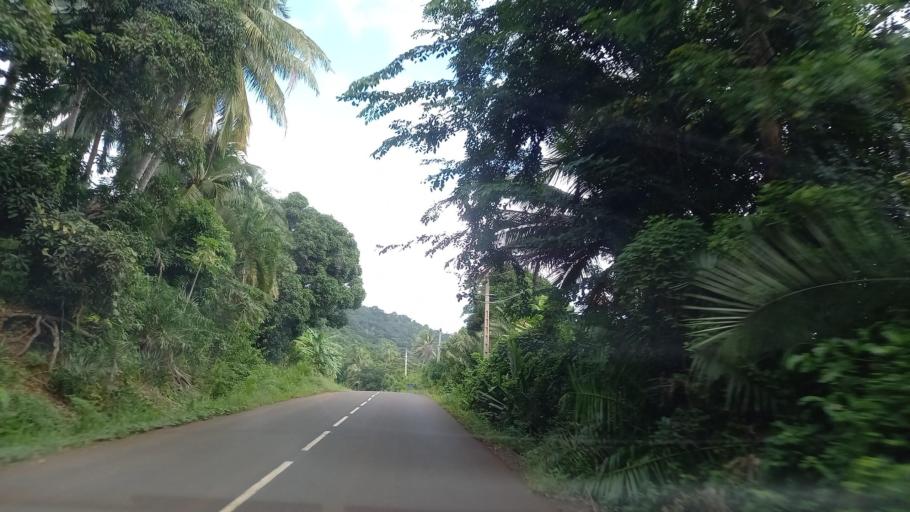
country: YT
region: Kani-Keli
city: Kani Keli
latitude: -12.9407
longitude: 45.1021
